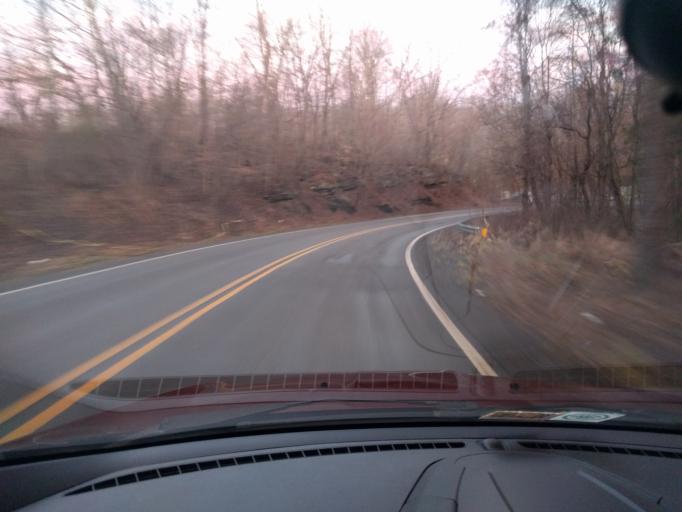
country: US
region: West Virginia
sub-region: Greenbrier County
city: Rainelle
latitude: 38.0226
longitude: -80.9162
